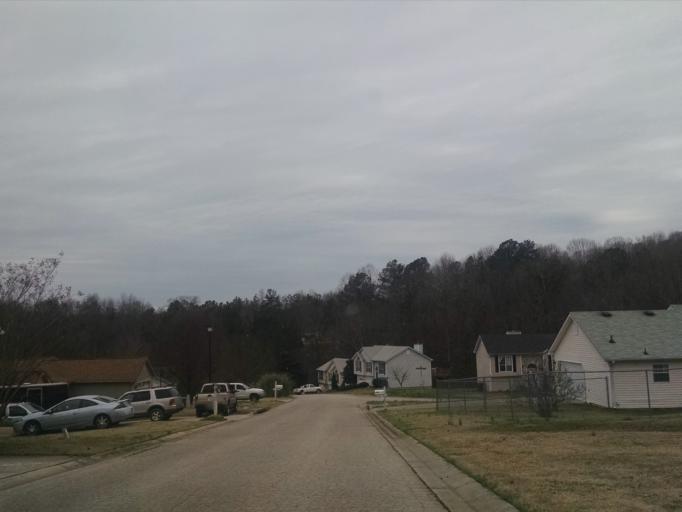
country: US
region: Georgia
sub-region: Hall County
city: Oakwood
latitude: 34.2036
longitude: -83.8617
